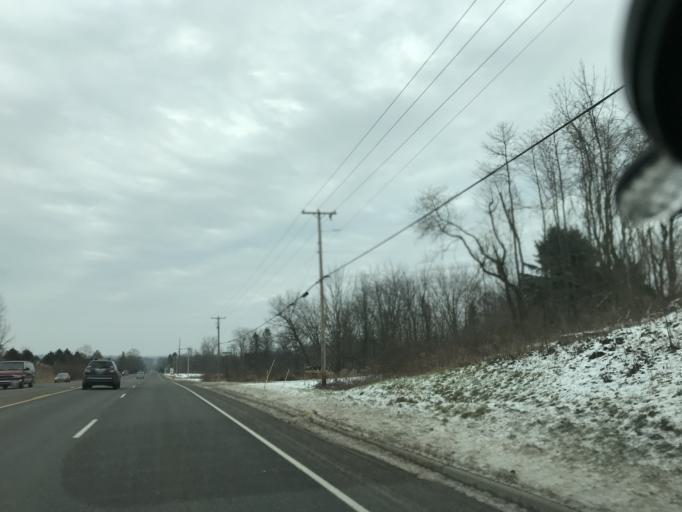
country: US
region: Michigan
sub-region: Kent County
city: Rockford
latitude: 43.1171
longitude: -85.5798
